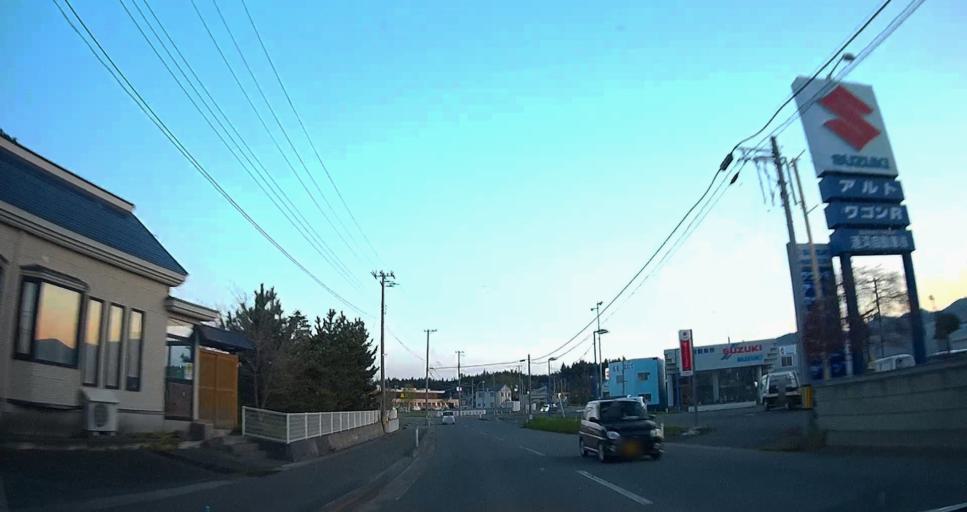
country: JP
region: Aomori
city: Misawa
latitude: 40.8694
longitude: 141.1121
